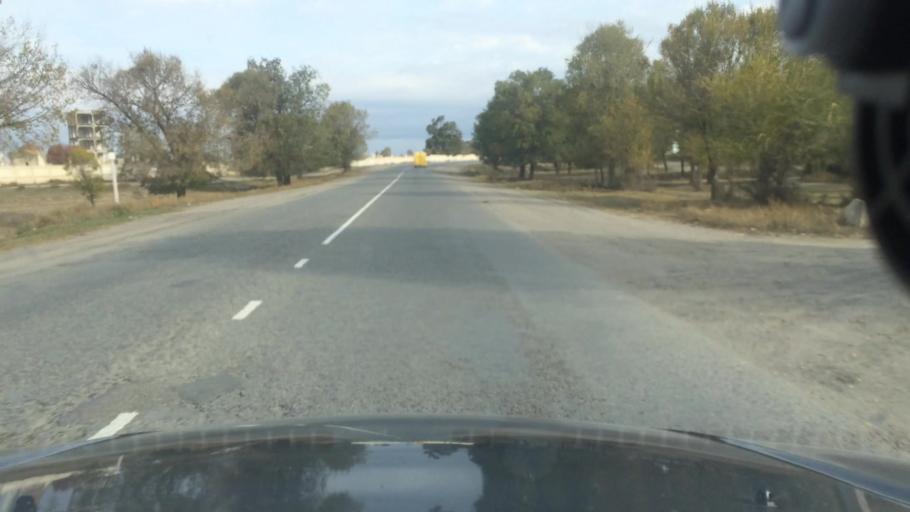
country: KG
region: Ysyk-Koel
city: Karakol
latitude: 42.5354
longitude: 78.3819
